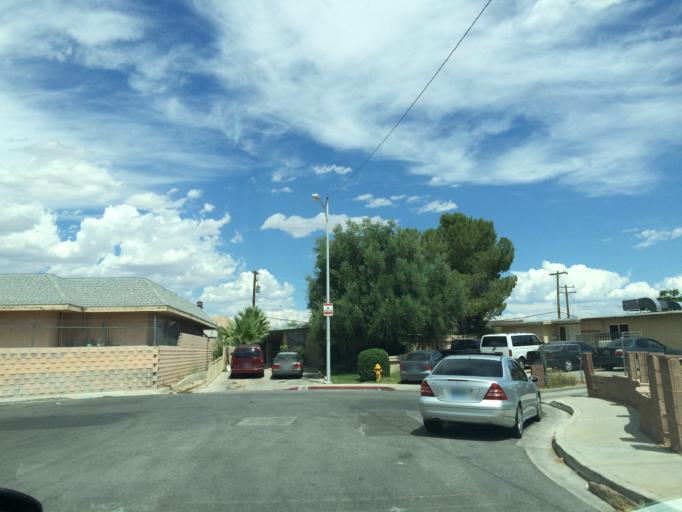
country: US
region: Nevada
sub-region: Clark County
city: North Las Vegas
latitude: 36.1944
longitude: -115.1232
